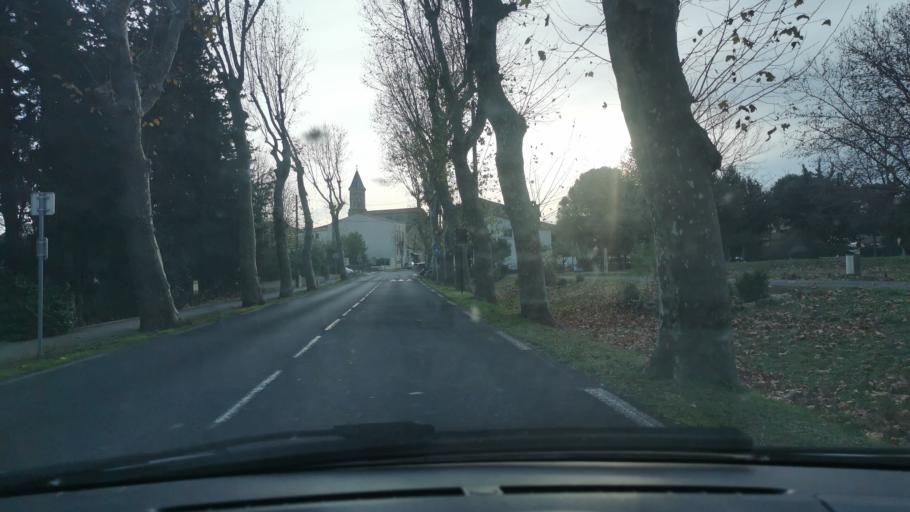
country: FR
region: Languedoc-Roussillon
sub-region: Departement de l'Herault
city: Mireval
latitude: 43.5103
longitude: 3.8029
